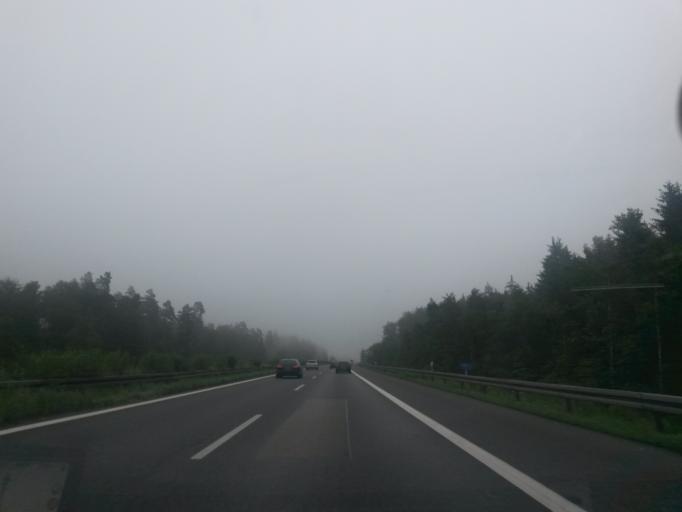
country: DE
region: Bavaria
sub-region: Regierungsbezirk Mittelfranken
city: Feucht
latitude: 49.4024
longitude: 11.2436
